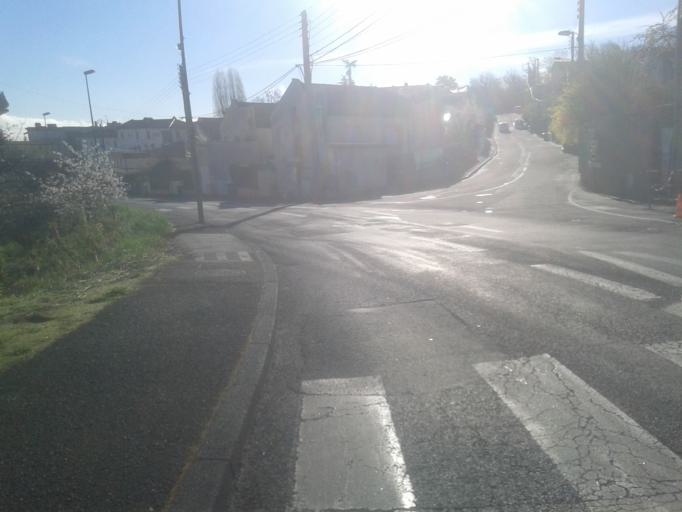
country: FR
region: Auvergne
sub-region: Departement du Puy-de-Dome
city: Chamalieres
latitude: 45.7666
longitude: 3.0664
